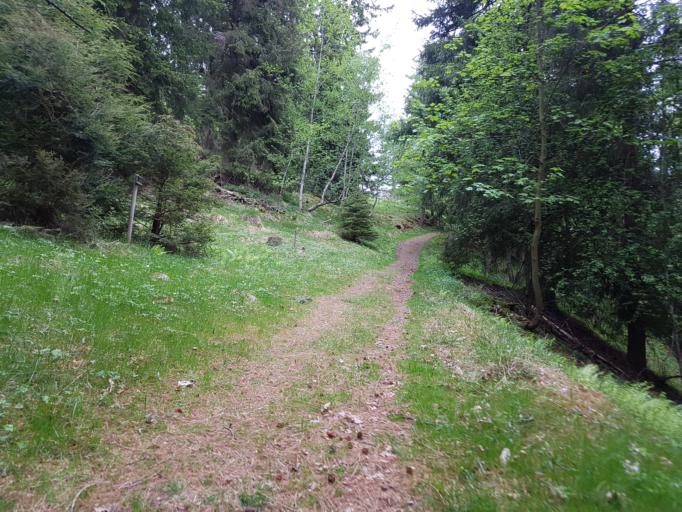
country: NO
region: Nord-Trondelag
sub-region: Levanger
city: Levanger
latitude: 63.7418
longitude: 11.2691
